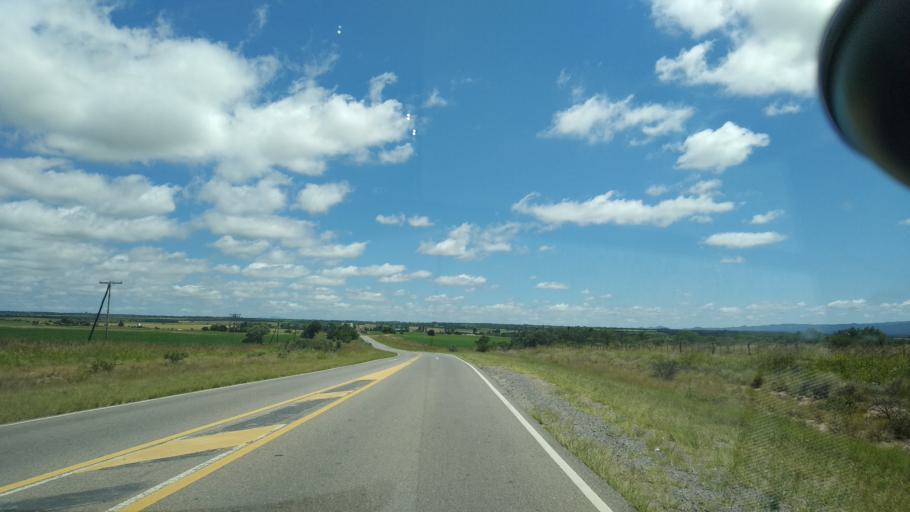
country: AR
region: Cordoba
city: Villa Cura Brochero
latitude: -31.6527
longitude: -65.0992
